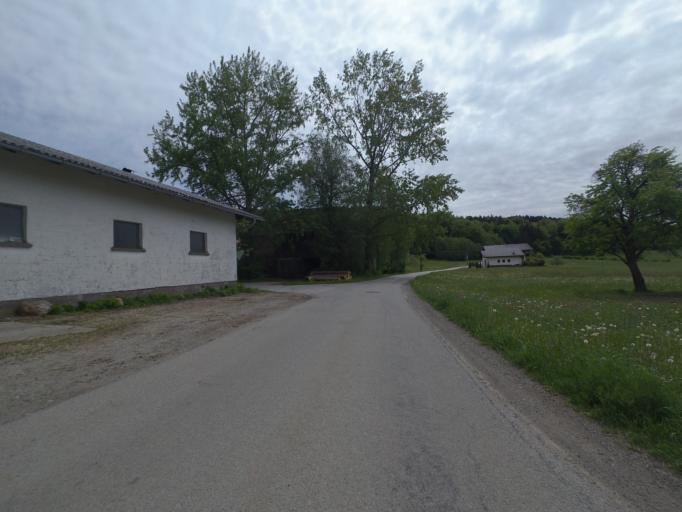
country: AT
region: Salzburg
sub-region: Politischer Bezirk Salzburg-Umgebung
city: Schleedorf
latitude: 47.9972
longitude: 13.1571
